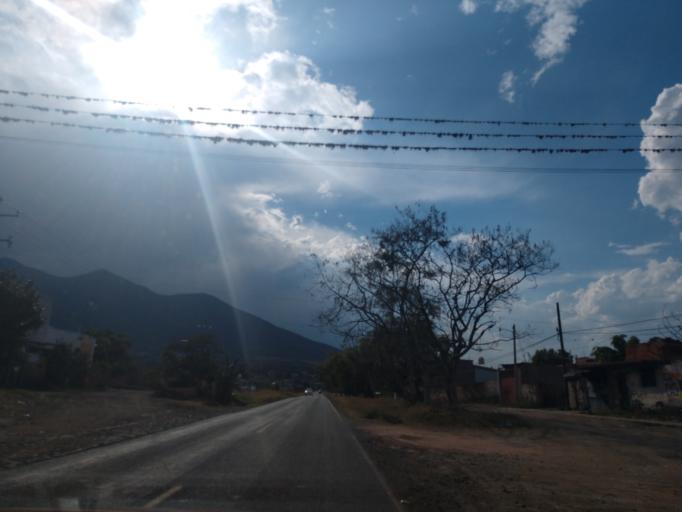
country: MX
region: Jalisco
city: San Juan Cosala
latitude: 20.1943
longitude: -103.2981
